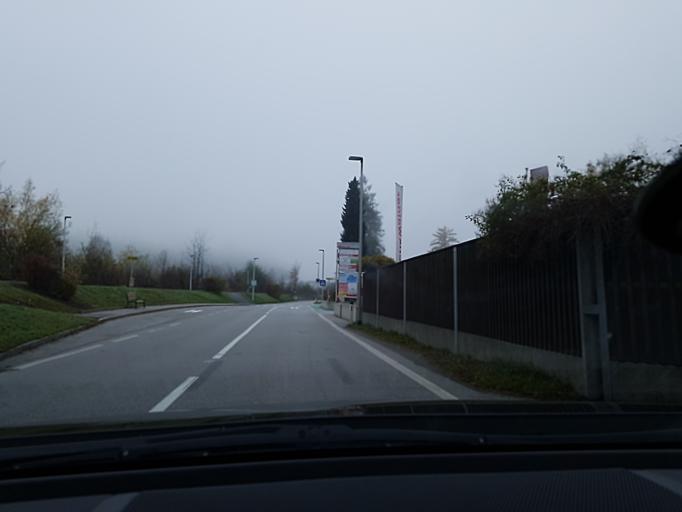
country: AT
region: Salzburg
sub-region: Politischer Bezirk Sankt Johann im Pongau
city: Sankt Johann im Pongau
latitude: 47.3549
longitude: 13.2010
